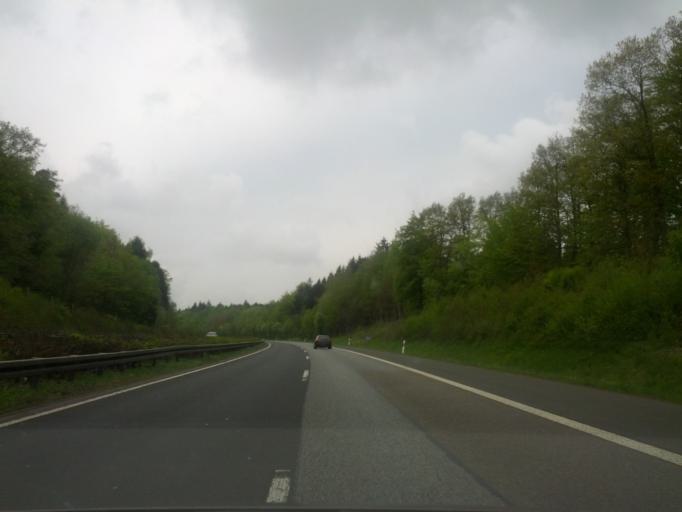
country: DE
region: Hesse
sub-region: Regierungsbezirk Giessen
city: Grossen Buseck
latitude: 50.6293
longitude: 8.7910
